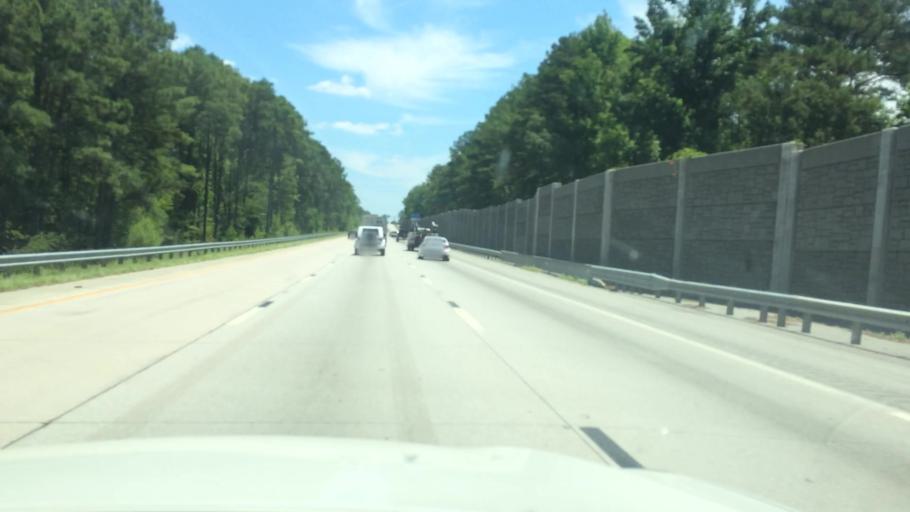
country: US
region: South Carolina
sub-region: Richland County
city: Woodfield
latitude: 34.0890
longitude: -80.8693
